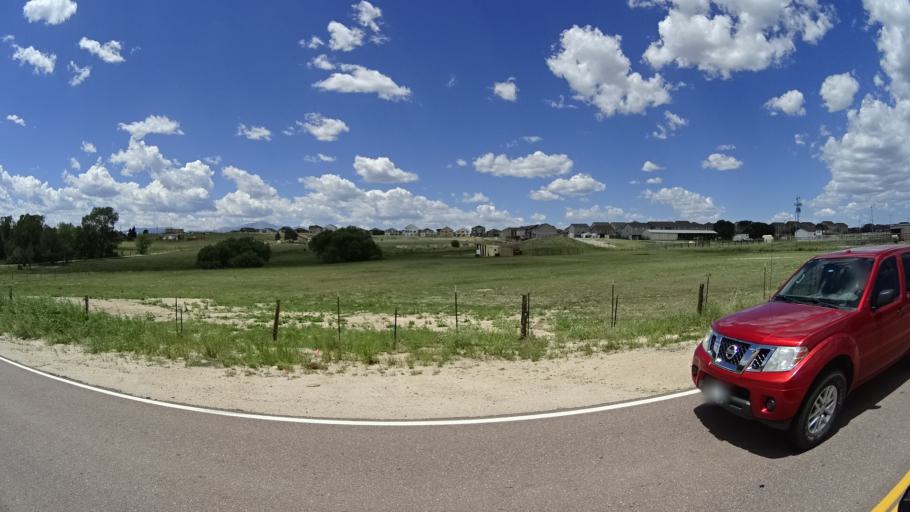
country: US
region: Colorado
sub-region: El Paso County
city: Black Forest
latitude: 38.9482
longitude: -104.7009
